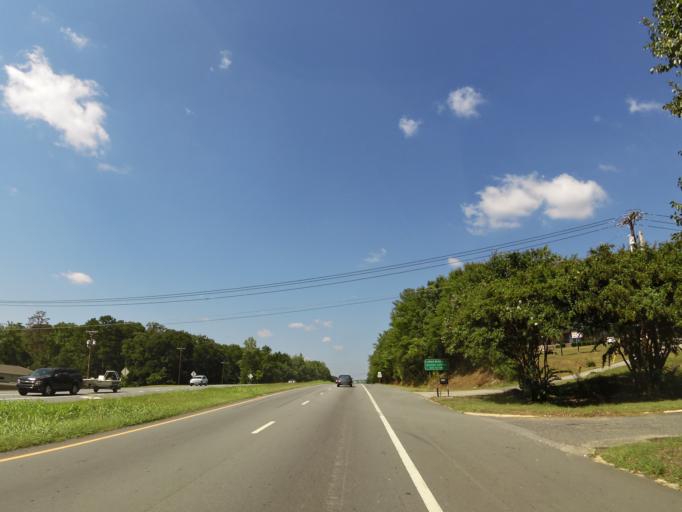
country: US
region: North Carolina
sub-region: Gaston County
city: Dallas
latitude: 35.2969
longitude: -81.1878
